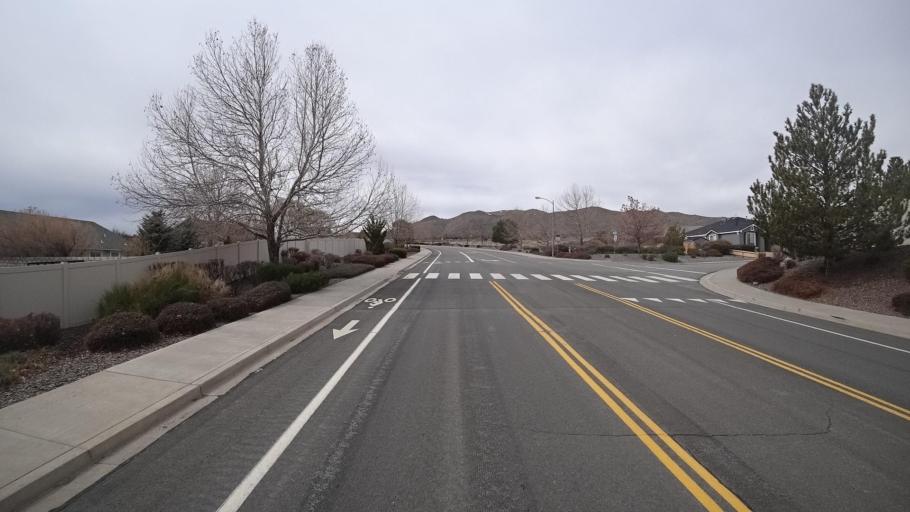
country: US
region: Nevada
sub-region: Washoe County
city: Spanish Springs
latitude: 39.6566
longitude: -119.7318
